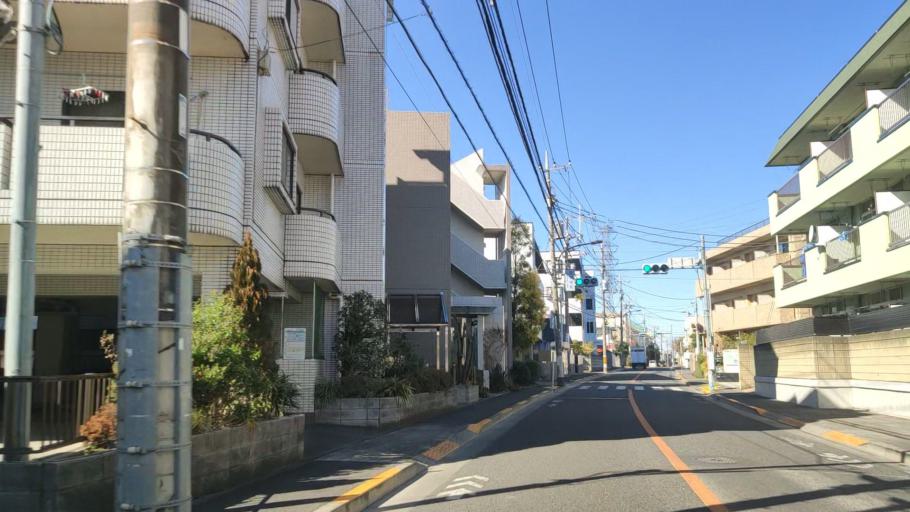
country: JP
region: Tokyo
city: Mitaka-shi
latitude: 35.6689
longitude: 139.5735
